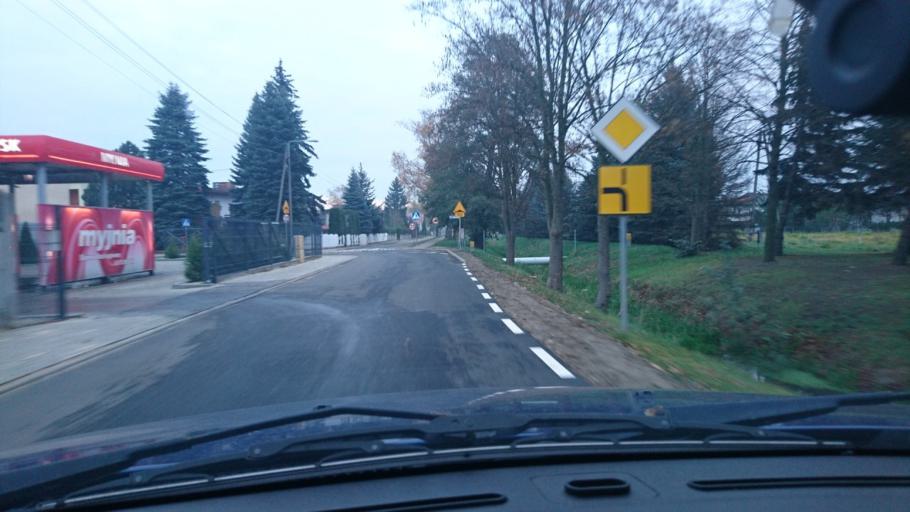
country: PL
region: Greater Poland Voivodeship
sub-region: Powiat ostrowski
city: Odolanow
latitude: 51.5737
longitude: 17.6768
